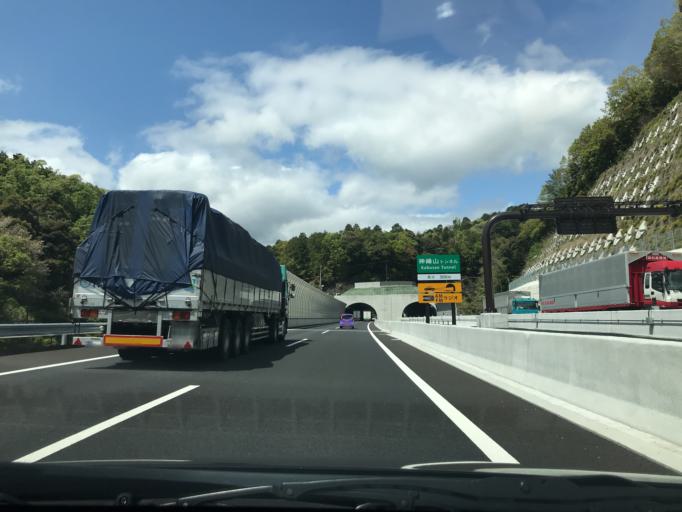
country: JP
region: Osaka
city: Takatsuki
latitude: 34.8927
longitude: 135.6087
